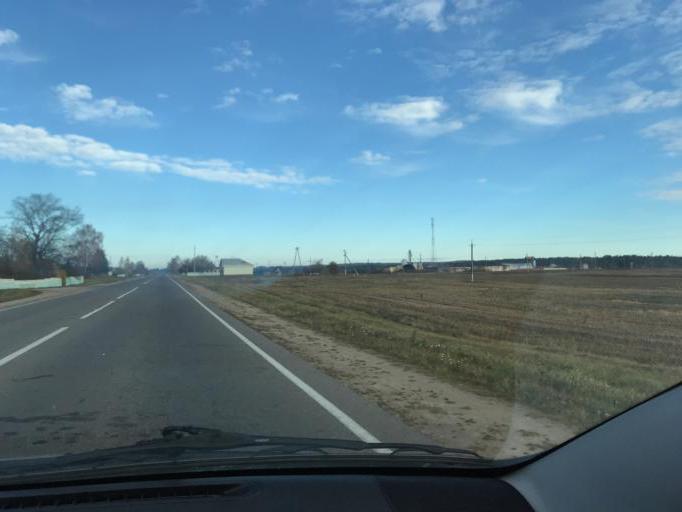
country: BY
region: Vitebsk
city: Haradok
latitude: 55.4818
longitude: 29.9683
